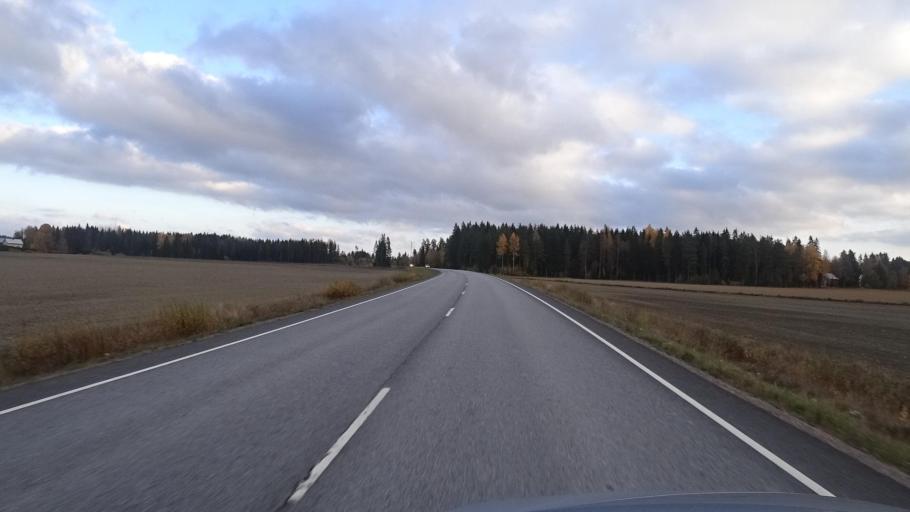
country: FI
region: Varsinais-Suomi
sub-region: Loimaa
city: Alastaro
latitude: 60.8828
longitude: 22.9782
